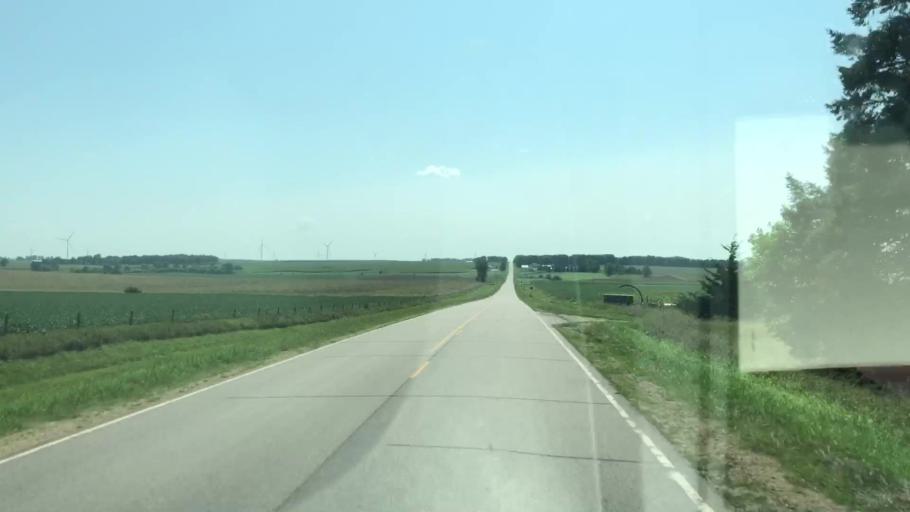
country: US
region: Iowa
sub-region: O'Brien County
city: Sanborn
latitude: 43.2495
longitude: -95.7235
